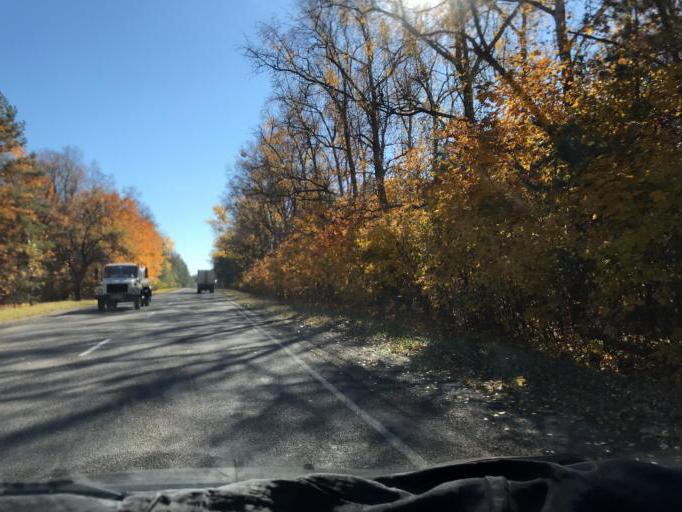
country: BY
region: Gomel
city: Kalinkavichy
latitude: 52.4494
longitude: 29.2743
